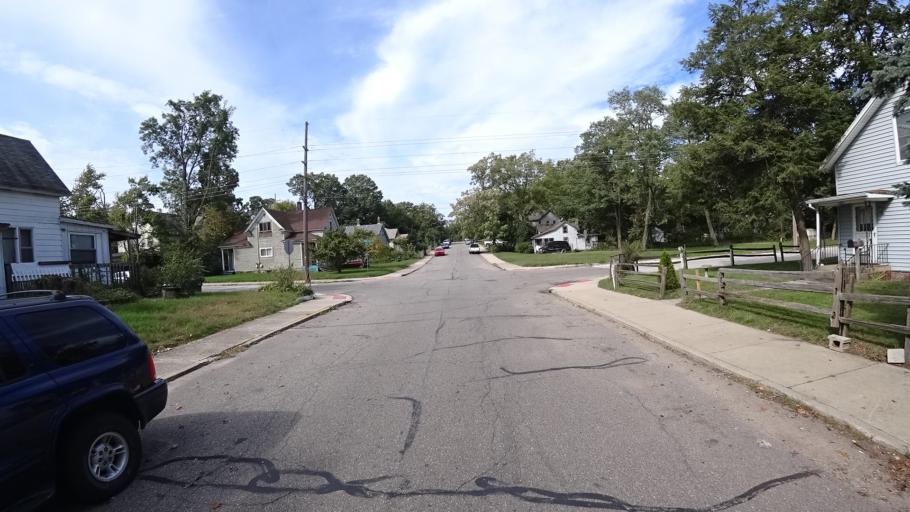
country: US
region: Indiana
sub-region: LaPorte County
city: Michigan City
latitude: 41.7146
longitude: -86.8875
